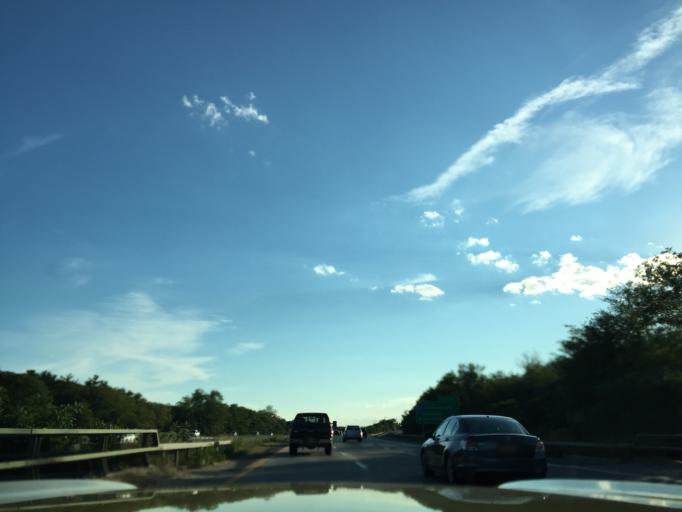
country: US
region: New York
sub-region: Suffolk County
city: Yaphank
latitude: 40.8339
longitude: -72.9115
